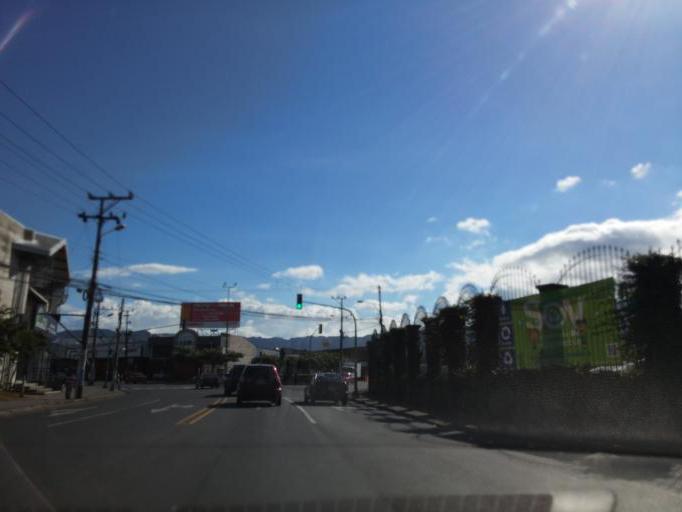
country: CR
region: San Jose
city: San Rafael Arriba
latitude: 9.9041
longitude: -84.0693
